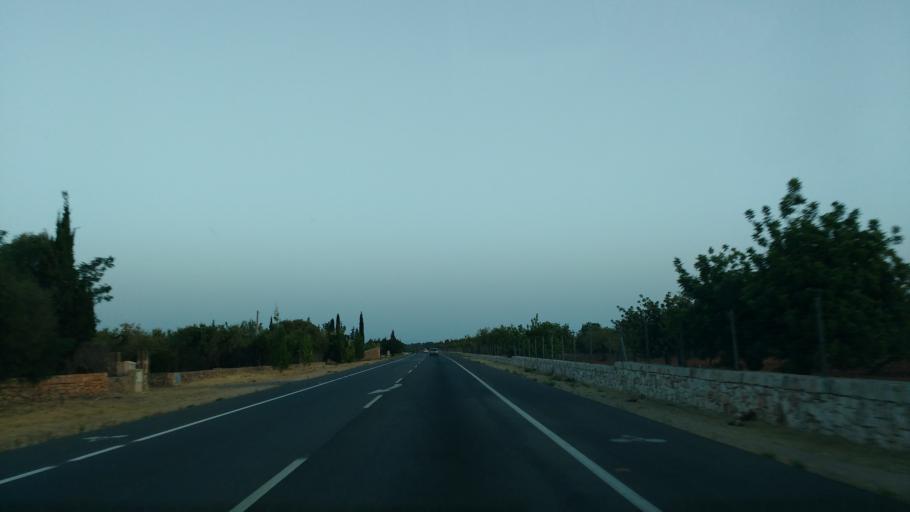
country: ES
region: Balearic Islands
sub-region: Illes Balears
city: Bunyola
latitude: 39.6633
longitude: 2.7149
